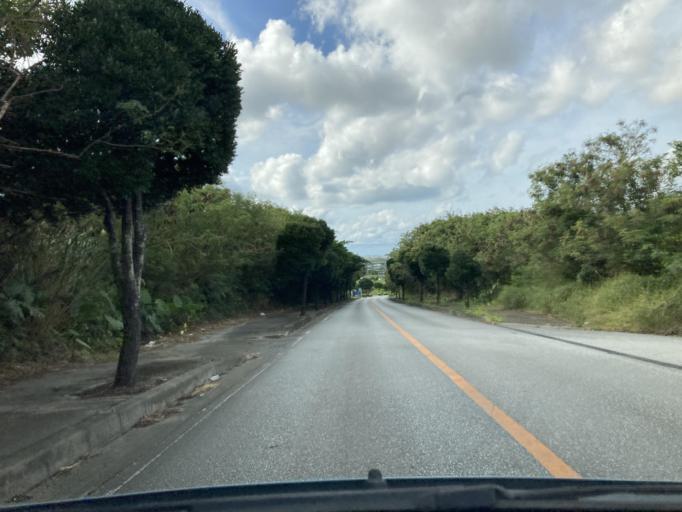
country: JP
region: Okinawa
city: Itoman
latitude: 26.1311
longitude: 127.7084
